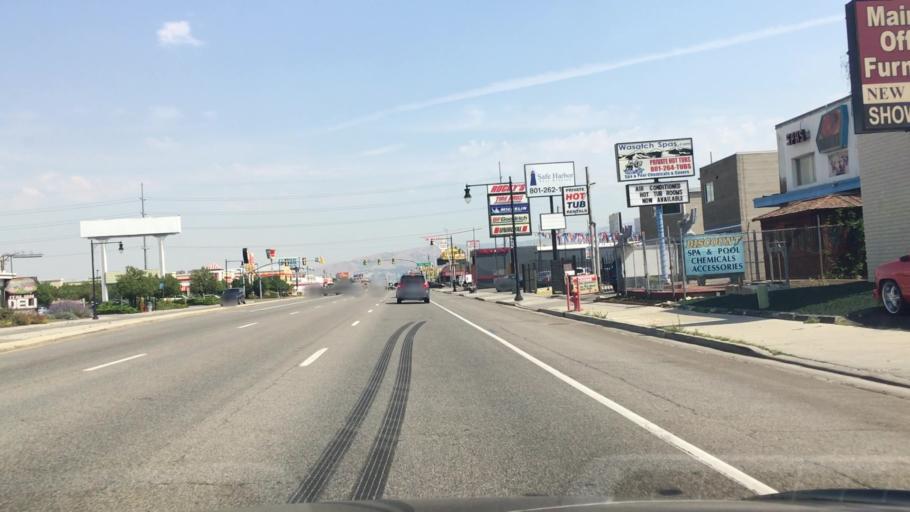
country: US
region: Utah
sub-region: Salt Lake County
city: Centerfield
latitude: 40.6854
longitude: -111.8882
